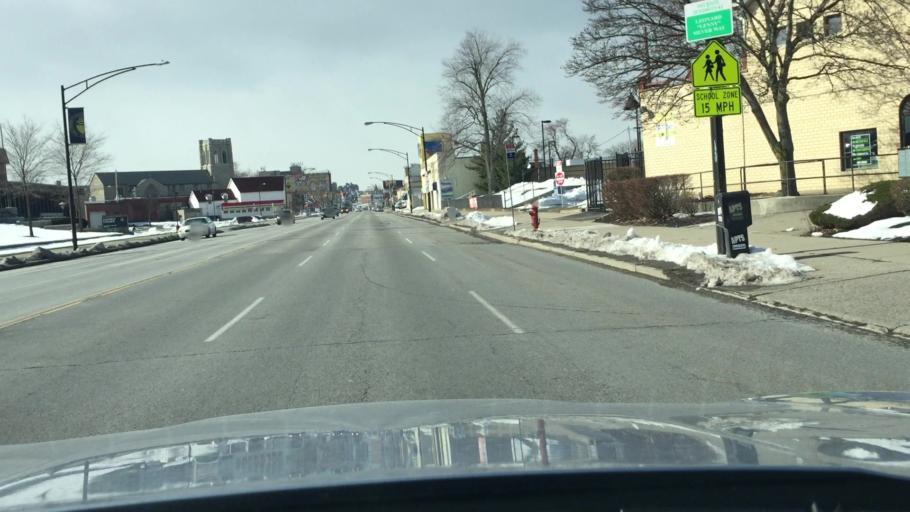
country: US
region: New York
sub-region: Erie County
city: Buffalo
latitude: 42.9220
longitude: -78.8576
